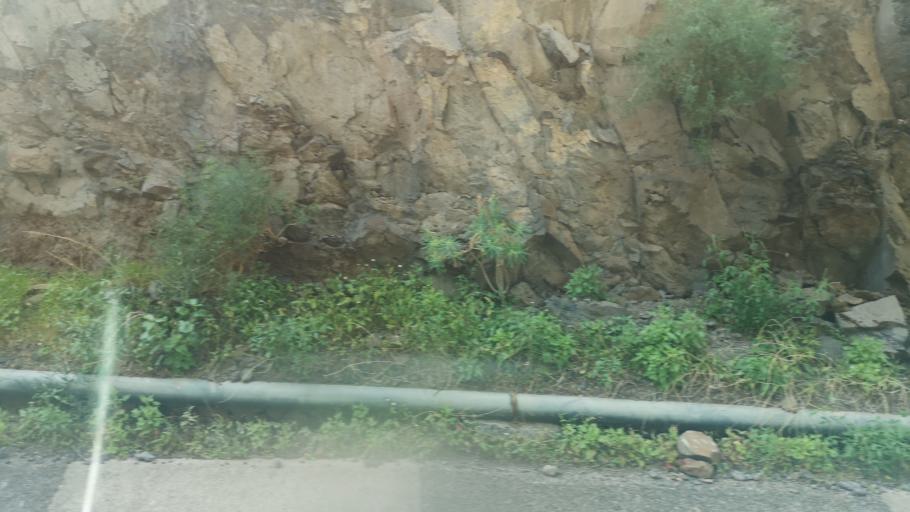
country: ES
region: Canary Islands
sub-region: Provincia de Santa Cruz de Tenerife
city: San Sebastian de la Gomera
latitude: 28.1130
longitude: -17.1346
